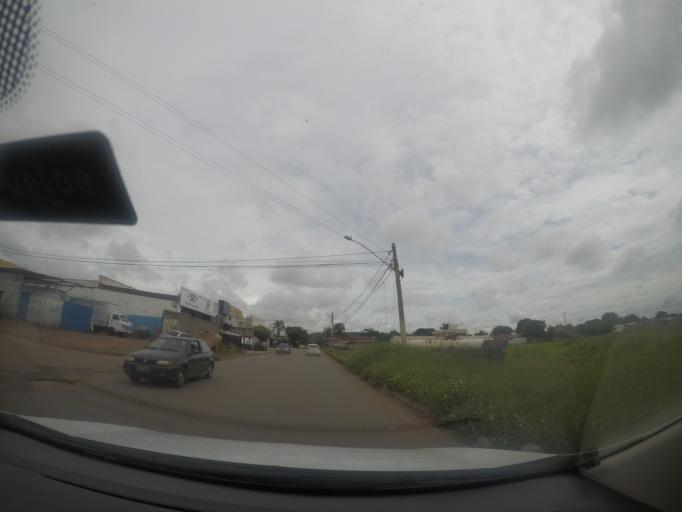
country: BR
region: Goias
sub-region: Goiania
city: Goiania
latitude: -16.6914
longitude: -49.3326
